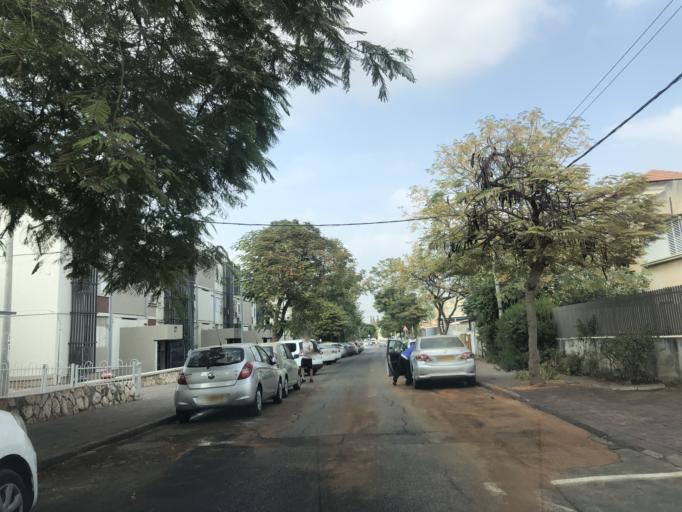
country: IL
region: Central District
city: Rosh Ha'Ayin
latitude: 32.0965
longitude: 34.9526
